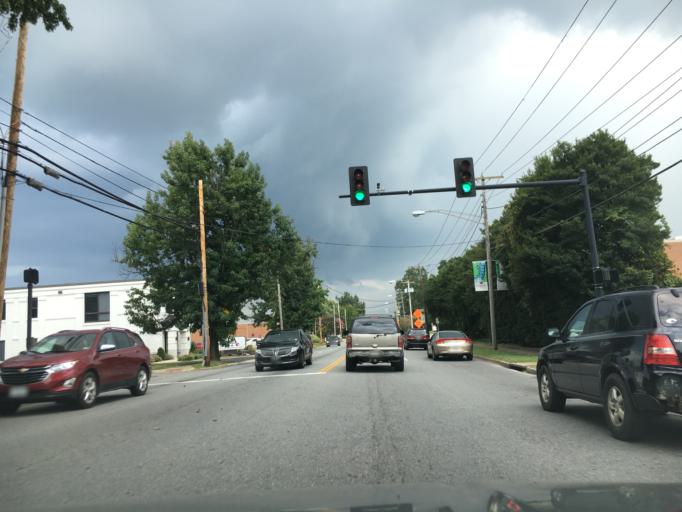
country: US
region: Virginia
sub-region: City of Lynchburg
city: West Lynchburg
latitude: 37.4104
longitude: -79.1678
